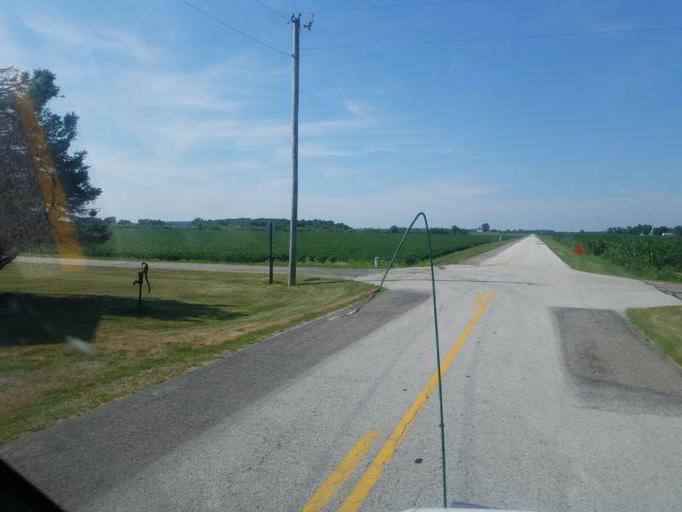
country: US
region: Ohio
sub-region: Logan County
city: Lakeview
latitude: 40.5483
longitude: -84.0120
